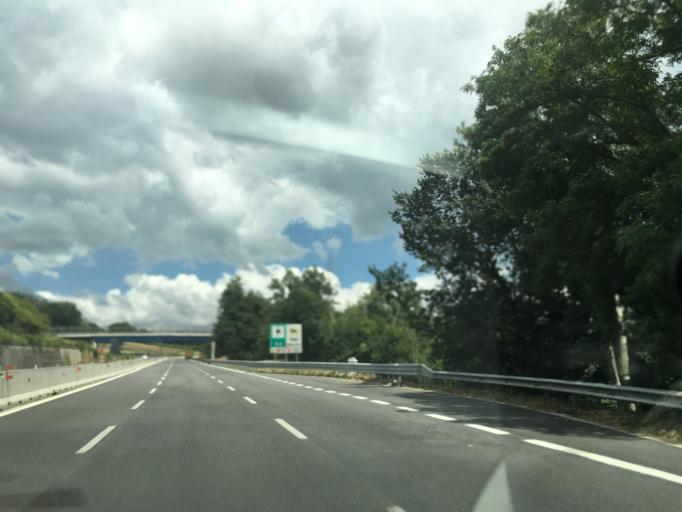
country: IT
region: Campania
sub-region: Provincia di Avellino
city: Campanarello
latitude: 41.0722
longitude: 14.9500
